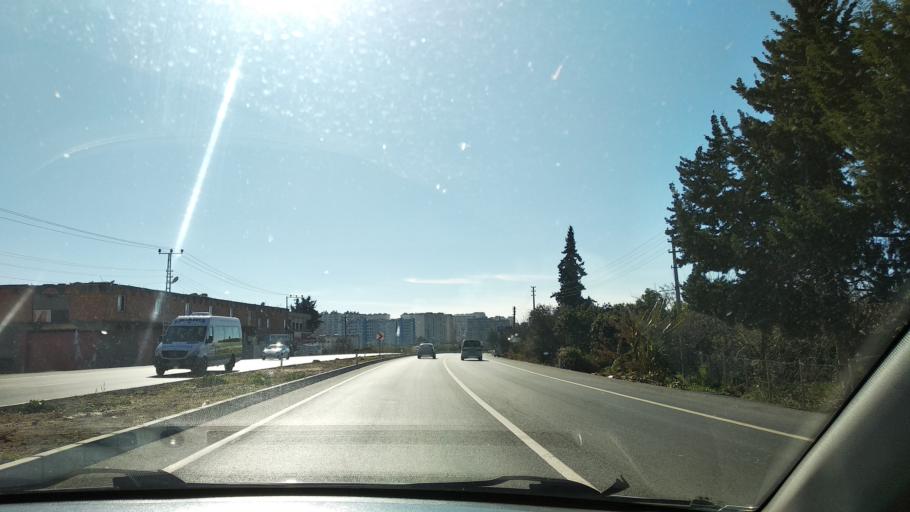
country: TR
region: Mersin
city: Tomuk
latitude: 36.6569
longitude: 34.3920
